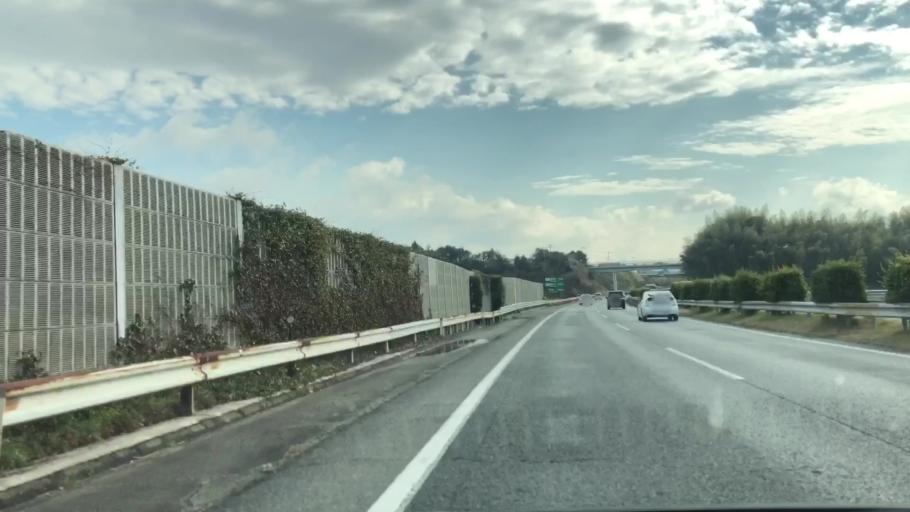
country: JP
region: Fukuoka
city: Setakamachi-takayanagi
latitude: 33.1359
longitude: 130.5158
